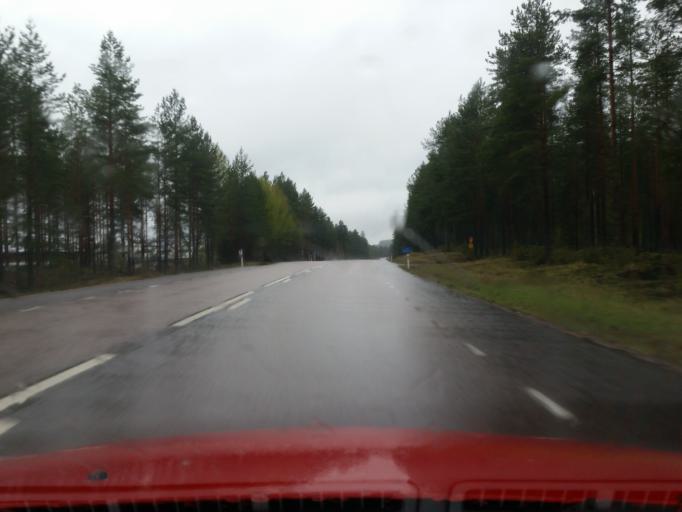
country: SE
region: Dalarna
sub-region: Leksand Municipality
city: Smedby
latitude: 60.6667
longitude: 15.0882
